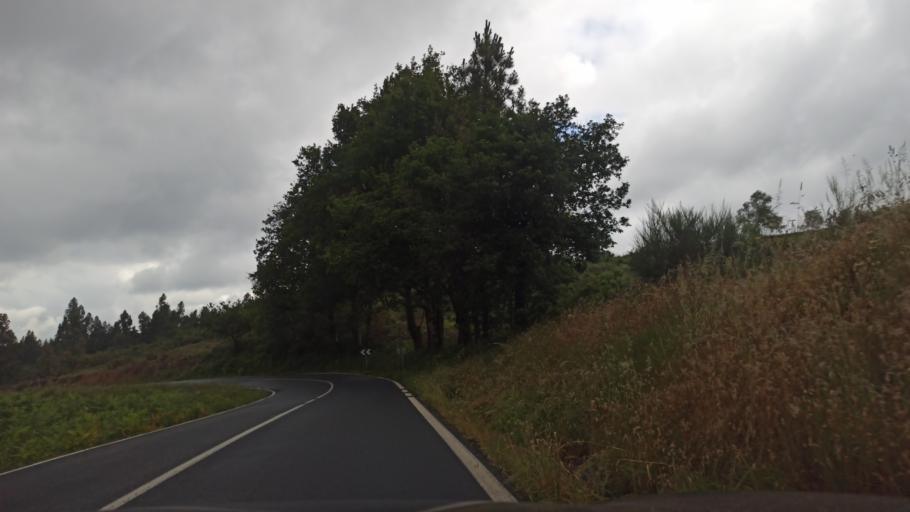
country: ES
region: Galicia
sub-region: Provincia da Coruna
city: Santiso
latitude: 42.7834
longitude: -8.0693
